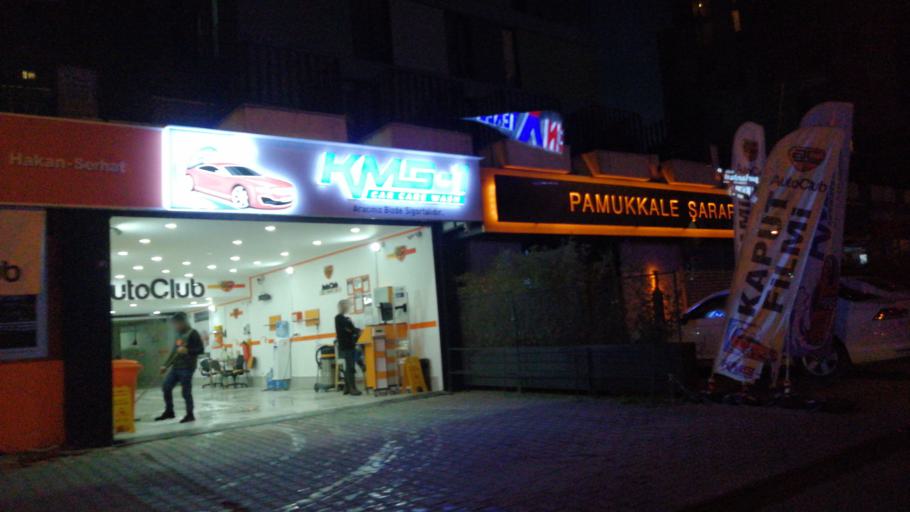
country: TR
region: Istanbul
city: Umraniye
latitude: 40.9991
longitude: 29.1415
